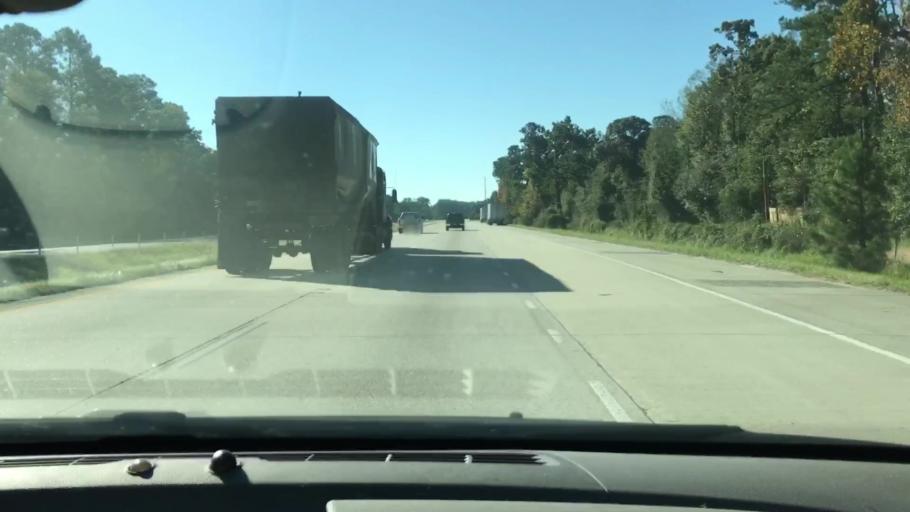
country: US
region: Louisiana
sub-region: Saint Tammany Parish
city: Pearl River
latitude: 30.3264
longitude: -89.7378
